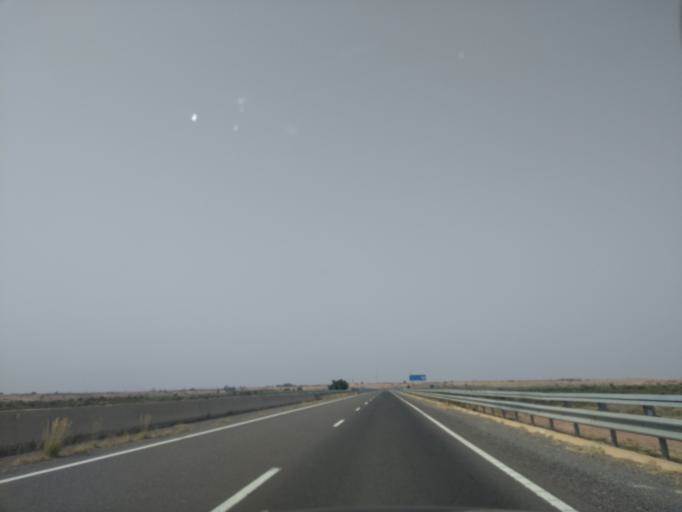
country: MA
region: Marrakech-Tensift-Al Haouz
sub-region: Marrakech
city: Marrakesh
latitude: 31.7343
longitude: -8.2167
